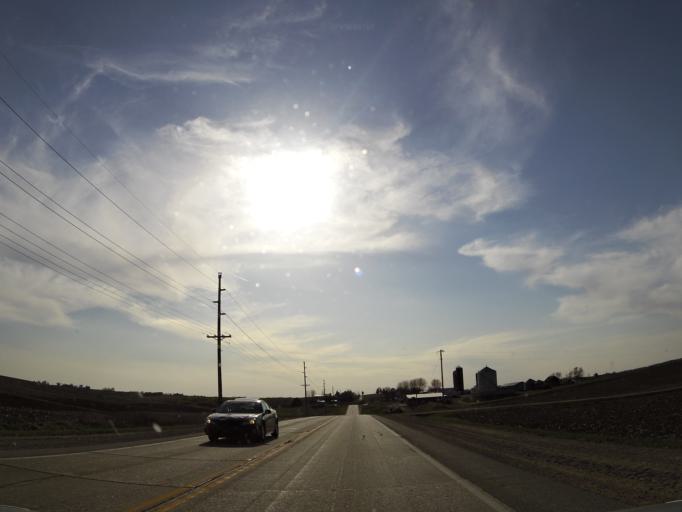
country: US
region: Wisconsin
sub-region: Pierce County
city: Ellsworth
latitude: 44.7319
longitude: -92.6159
